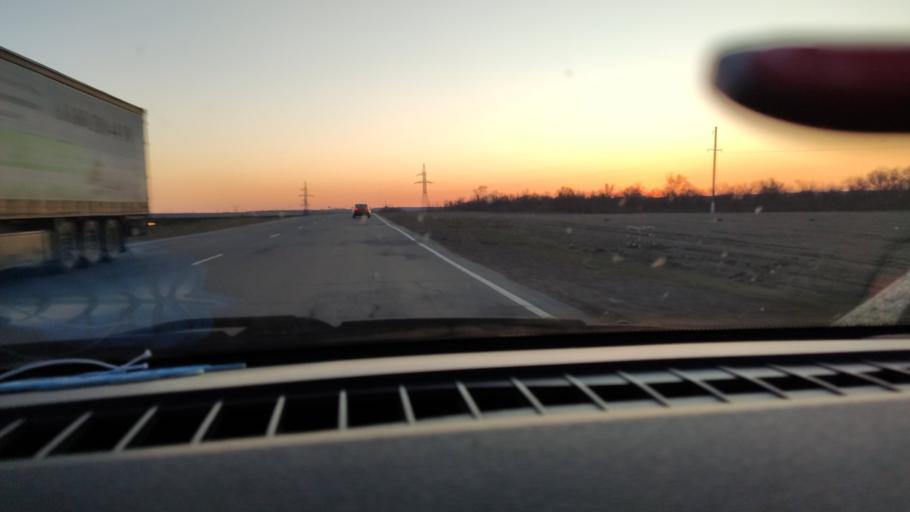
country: RU
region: Saratov
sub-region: Saratovskiy Rayon
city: Saratov
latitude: 51.7446
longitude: 46.0508
